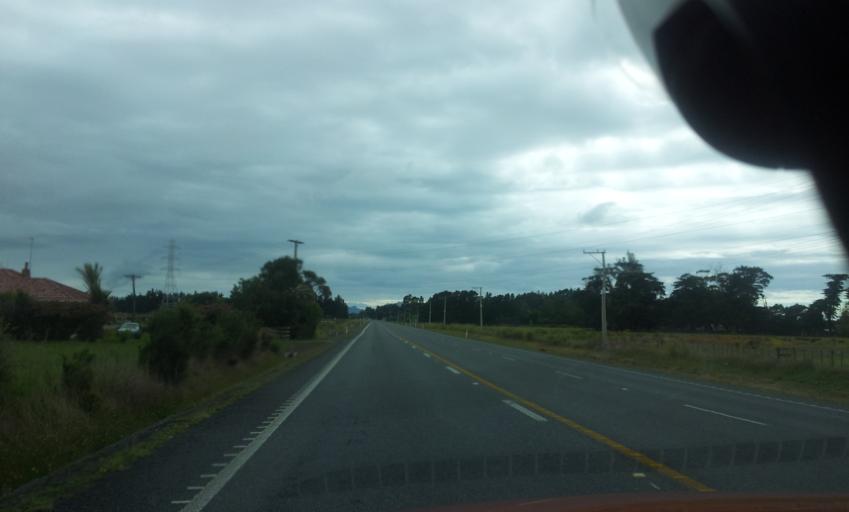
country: NZ
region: Northland
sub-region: Whangarei
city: Ruakaka
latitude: -35.9918
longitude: 174.4229
